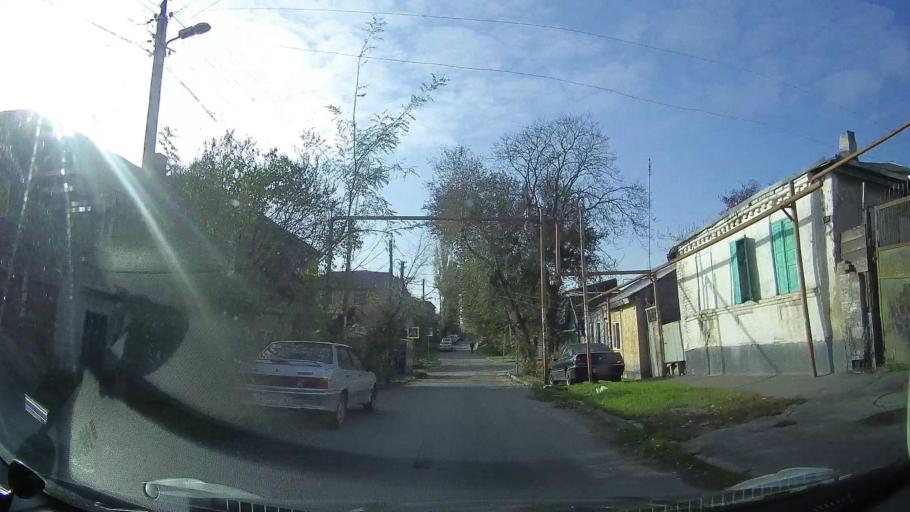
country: RU
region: Rostov
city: Rostov-na-Donu
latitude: 47.2214
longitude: 39.7397
